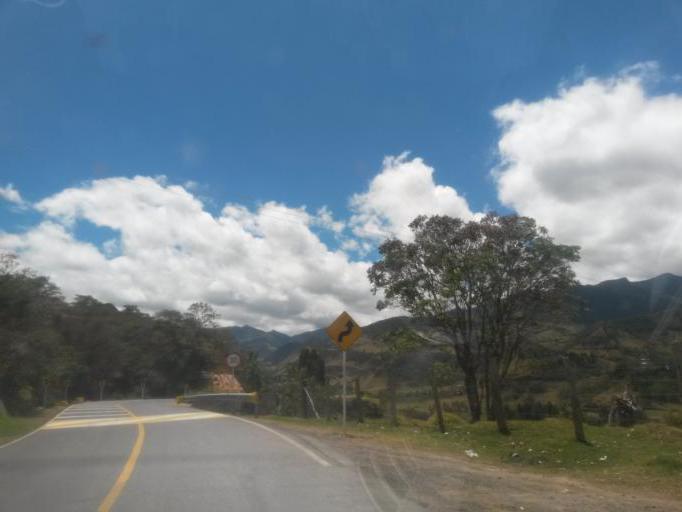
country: CO
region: Cauca
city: Silvia
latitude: 2.6027
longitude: -76.3946
